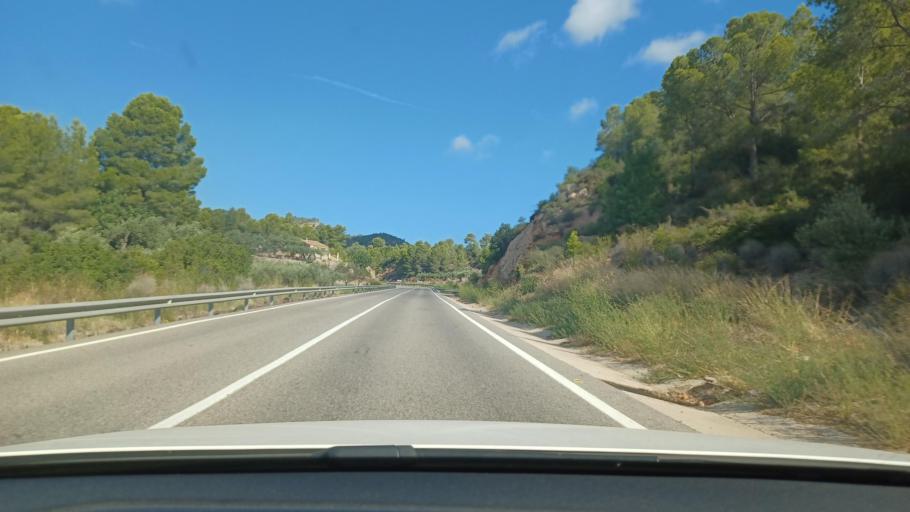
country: ES
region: Catalonia
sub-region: Provincia de Tarragona
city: Tivenys
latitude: 40.9389
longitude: 0.4670
